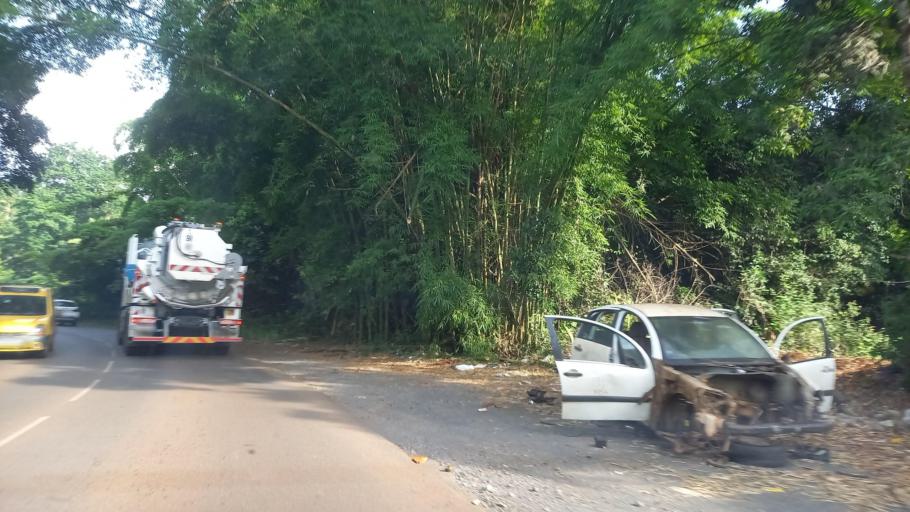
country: YT
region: Chiconi
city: Chiconi
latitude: -12.8079
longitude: 45.1271
